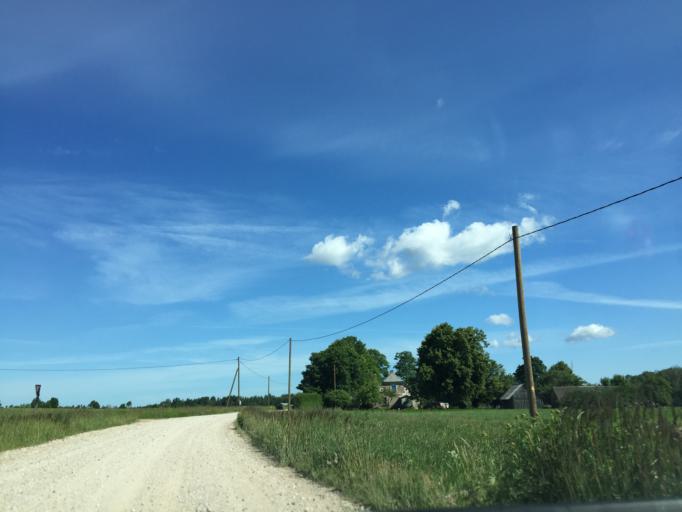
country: LV
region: Dundaga
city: Dundaga
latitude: 57.3476
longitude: 22.0259
